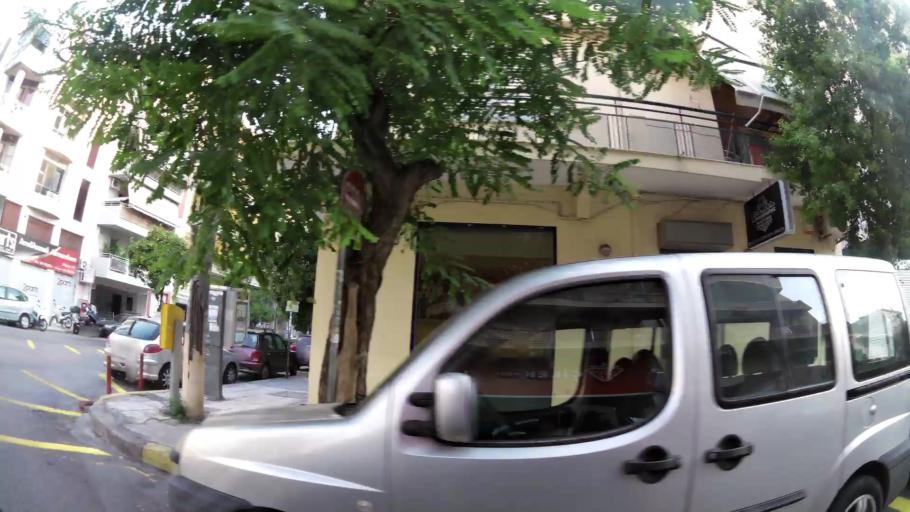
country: GR
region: Attica
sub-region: Nomarchia Athinas
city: Kallithea
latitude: 37.9501
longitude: 23.7066
